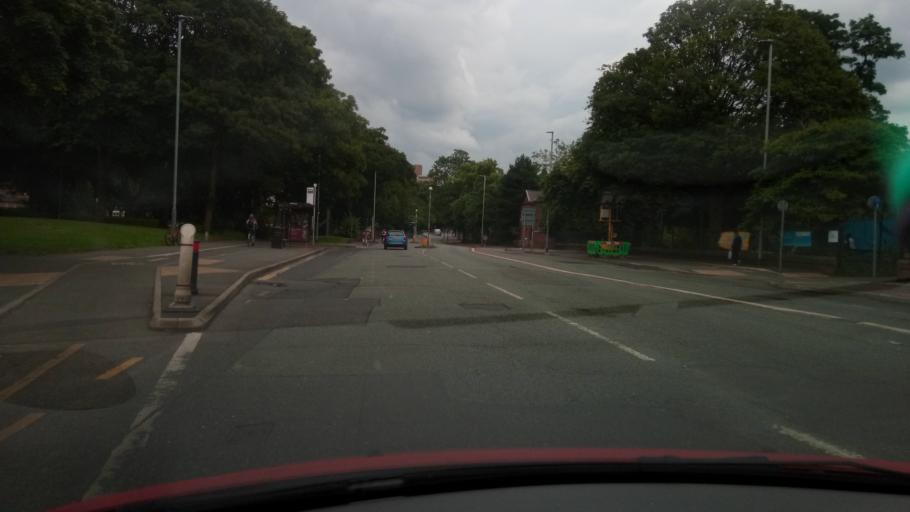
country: GB
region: England
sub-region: Manchester
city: Fallowfield
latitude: 53.4510
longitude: -2.2217
